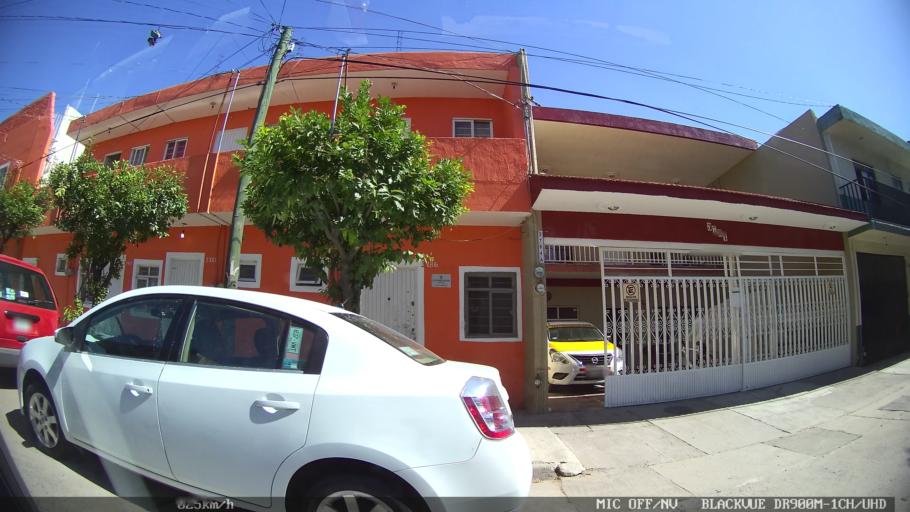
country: MX
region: Jalisco
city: Tlaquepaque
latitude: 20.6562
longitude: -103.2856
